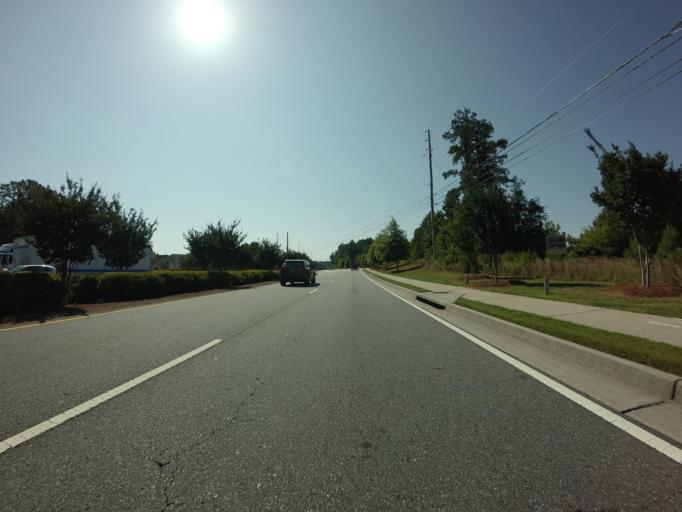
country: US
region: Georgia
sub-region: Fulton County
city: Johns Creek
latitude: 34.0606
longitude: -84.1556
